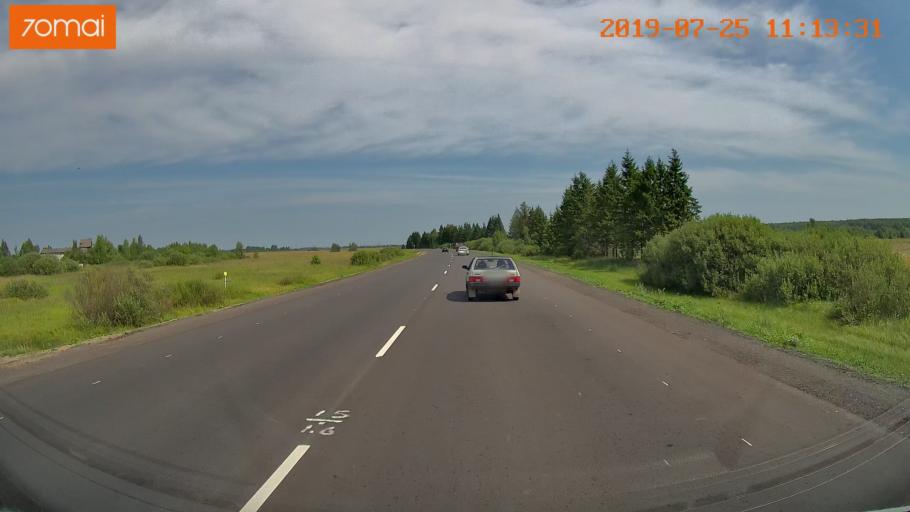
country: RU
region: Ivanovo
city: Privolzhsk
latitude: 57.3272
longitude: 41.2402
